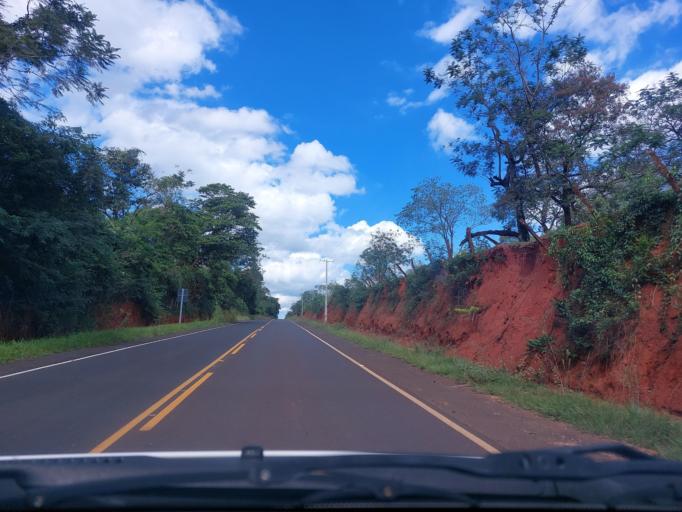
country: PY
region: San Pedro
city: Guayaybi
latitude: -24.5525
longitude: -56.5196
